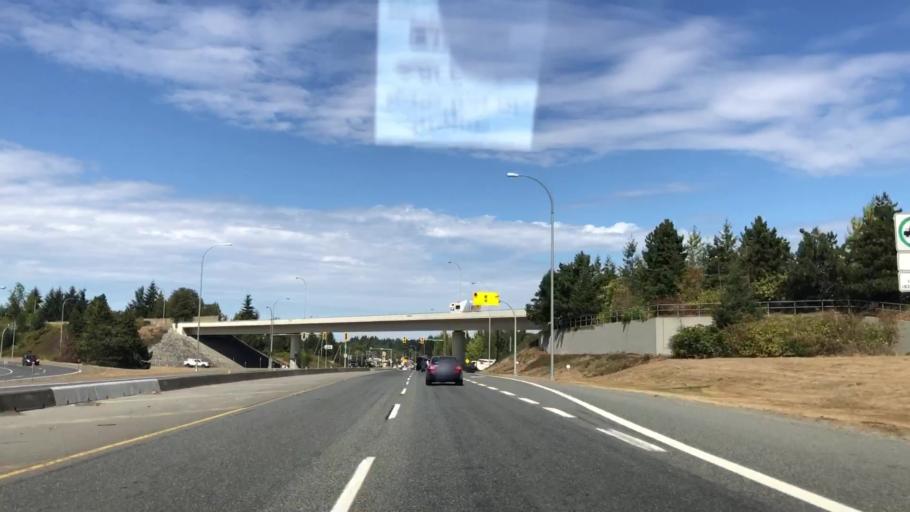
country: CA
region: British Columbia
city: Nanaimo
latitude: 49.1233
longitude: -123.9152
